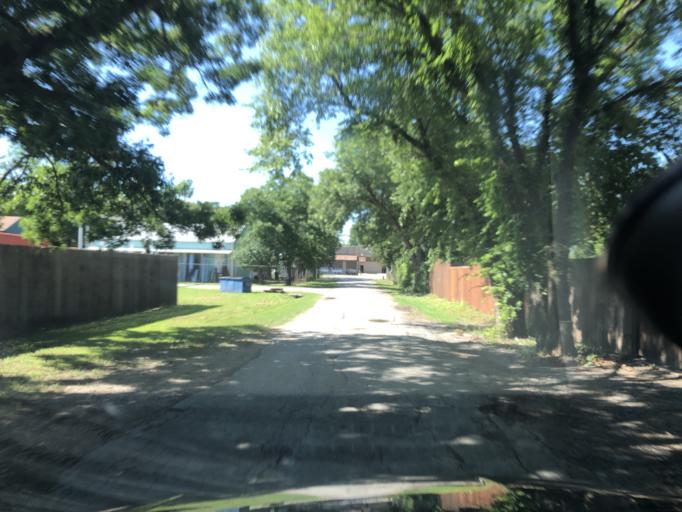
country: US
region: Texas
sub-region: Dallas County
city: Grand Prairie
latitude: 32.8045
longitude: -97.0218
